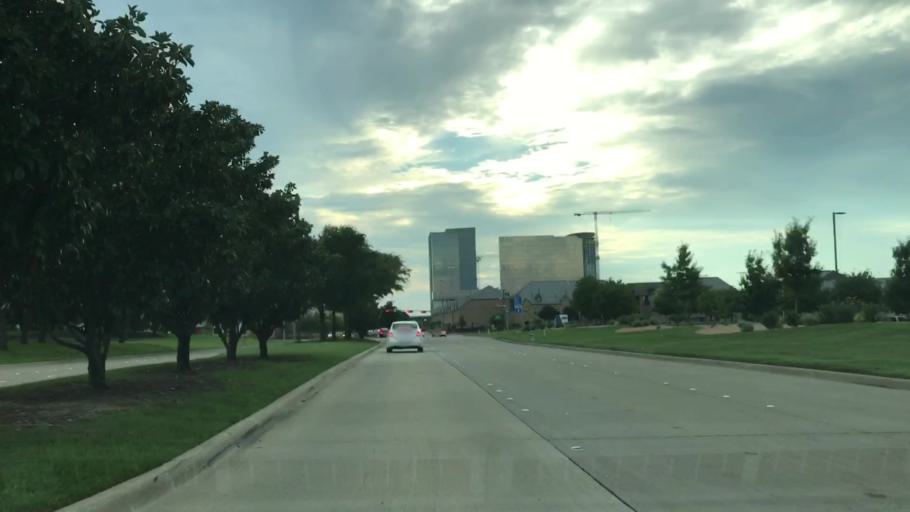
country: US
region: Texas
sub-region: Collin County
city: Frisco
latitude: 33.0842
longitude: -96.8165
